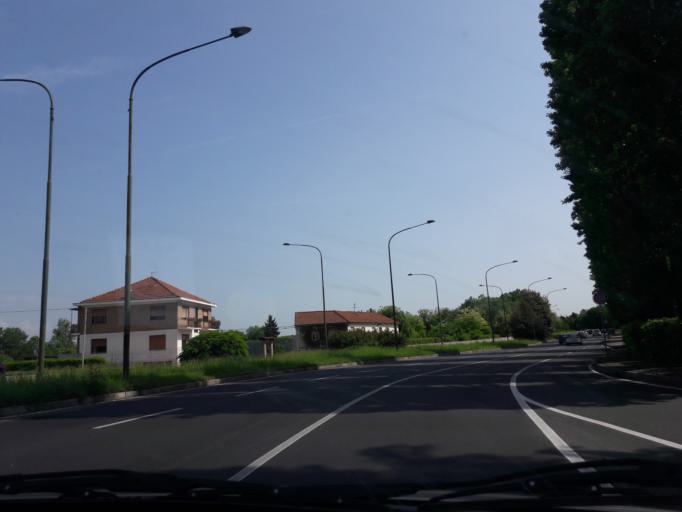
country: IT
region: Piedmont
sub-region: Provincia di Torino
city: Savonera
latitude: 45.0873
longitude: 7.6265
